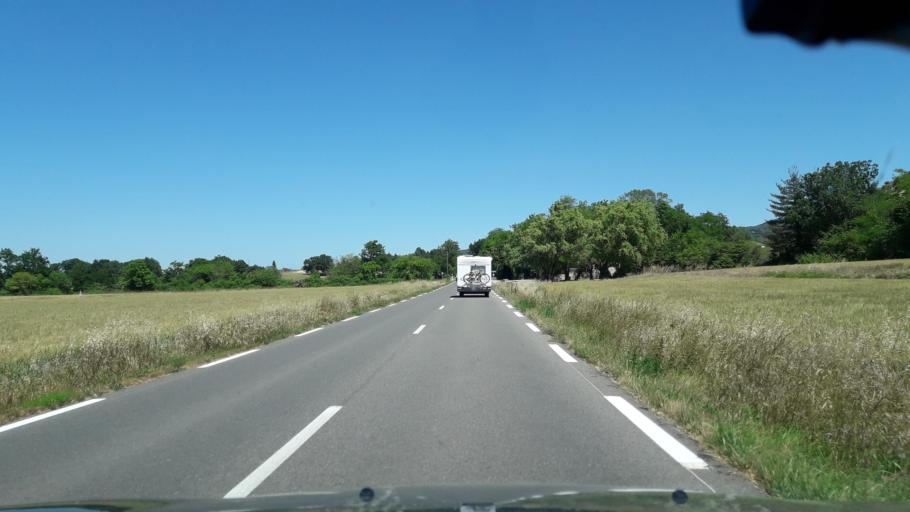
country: FR
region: Rhone-Alpes
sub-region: Departement de l'Ardeche
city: Lablachere
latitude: 44.3889
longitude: 4.2533
